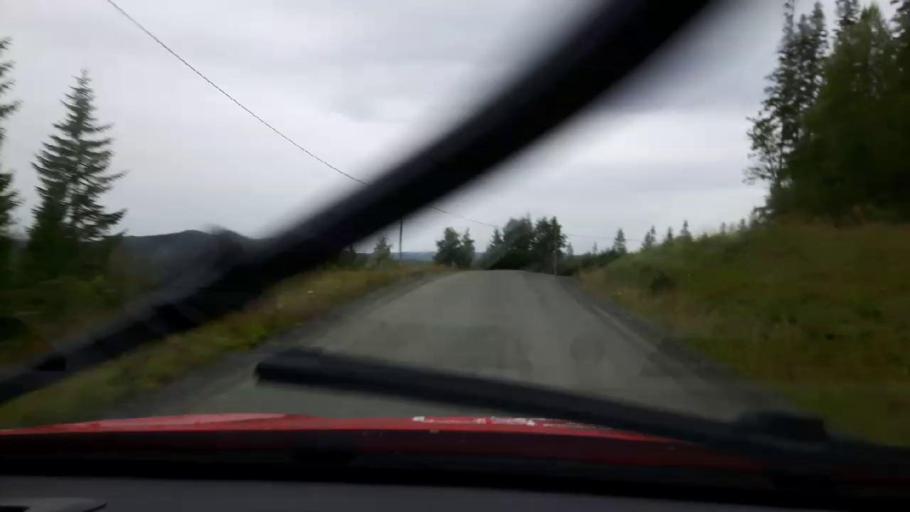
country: SE
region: Jaemtland
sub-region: Are Kommun
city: Are
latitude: 63.4190
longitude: 12.8248
